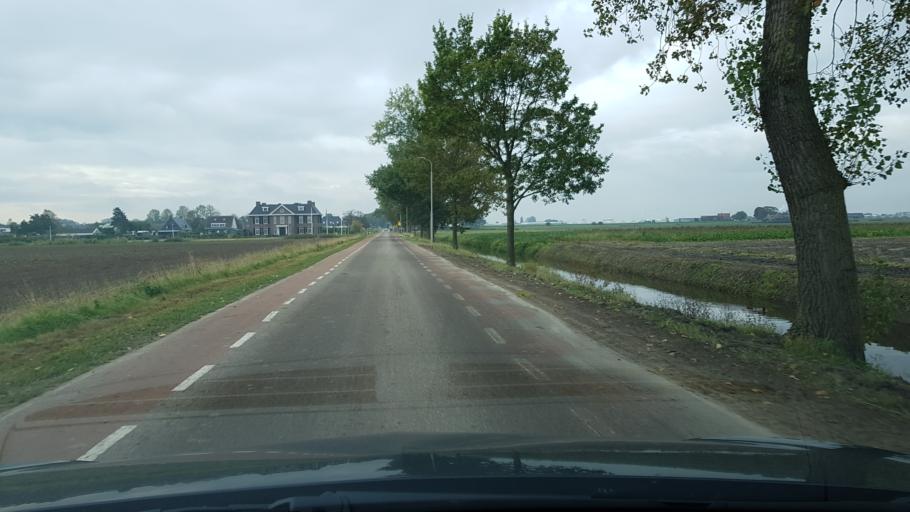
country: NL
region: North Holland
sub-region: Gemeente Aalsmeer
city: Aalsmeer
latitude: 52.2499
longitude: 4.7914
